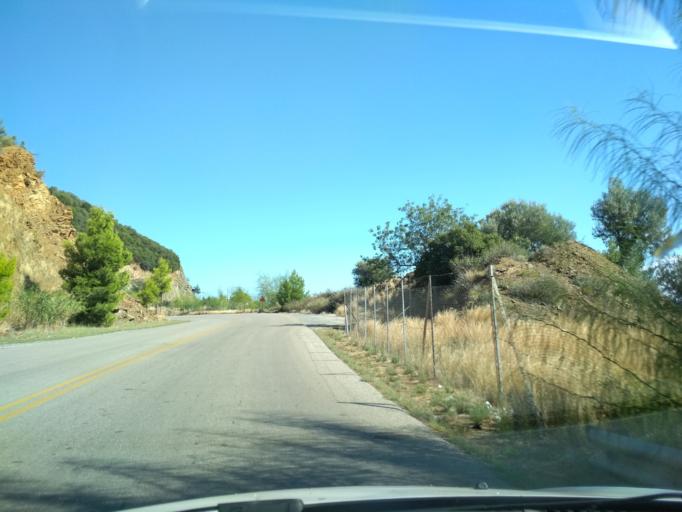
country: GR
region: Central Greece
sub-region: Nomos Evvoias
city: Oreoi
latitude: 38.8492
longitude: 23.0653
